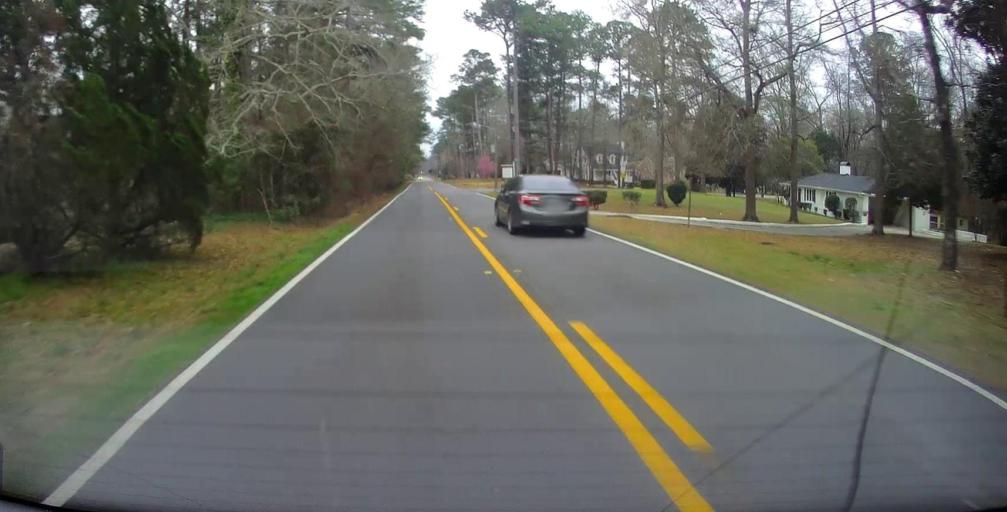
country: US
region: Georgia
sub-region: Bibb County
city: Macon
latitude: 32.9045
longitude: -83.7387
